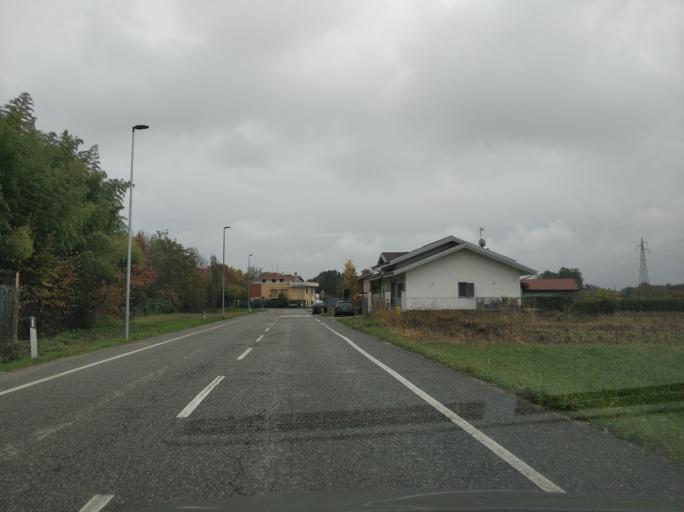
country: IT
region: Piedmont
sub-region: Provincia di Torino
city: Villanova Canavese
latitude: 45.2404
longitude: 7.5544
